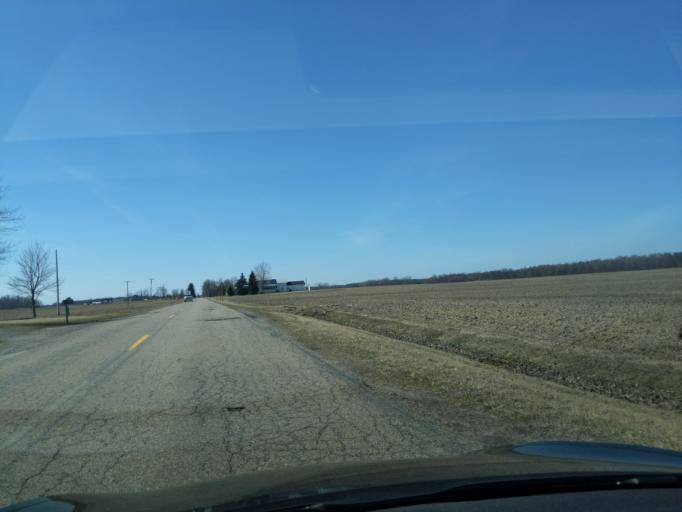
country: US
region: Michigan
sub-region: Ionia County
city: Portland
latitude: 42.7266
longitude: -84.9318
